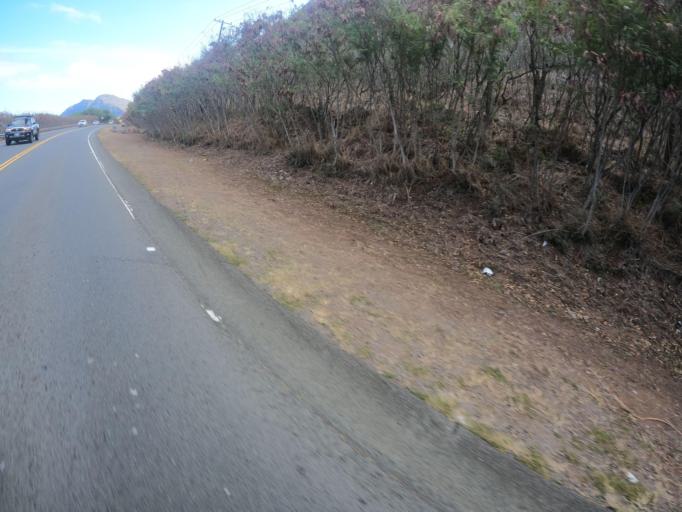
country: US
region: Hawaii
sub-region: Honolulu County
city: Waimanalo Beach
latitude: 21.3216
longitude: -157.6741
